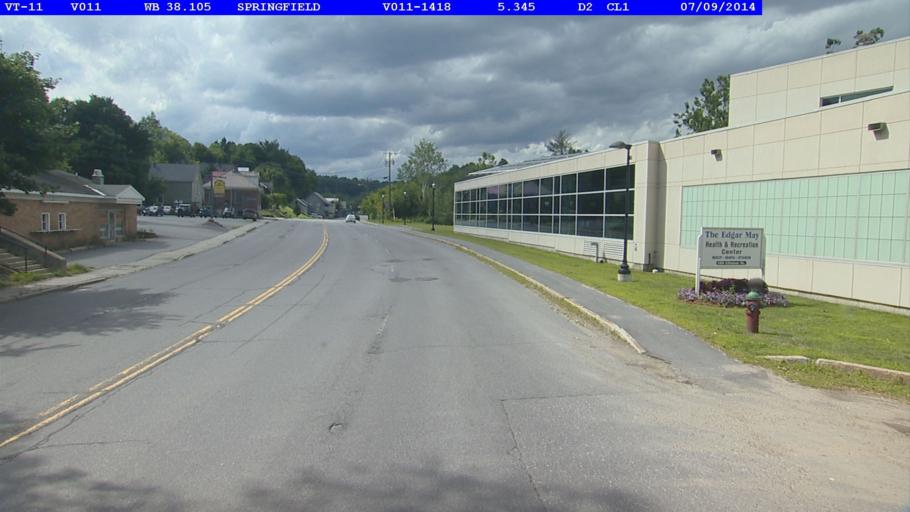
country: US
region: Vermont
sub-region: Windsor County
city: Springfield
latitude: 43.2913
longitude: -72.4734
